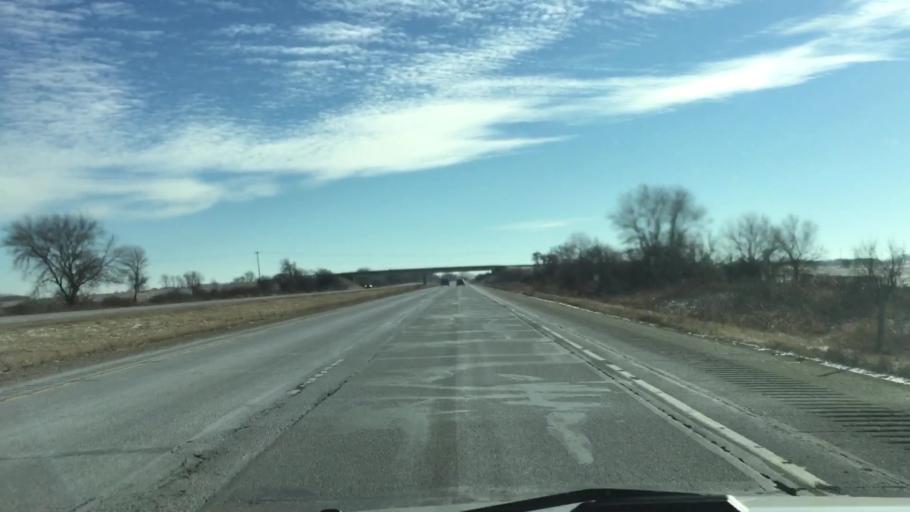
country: US
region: Wisconsin
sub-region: Walworth County
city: Como
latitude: 42.6402
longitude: -88.4906
